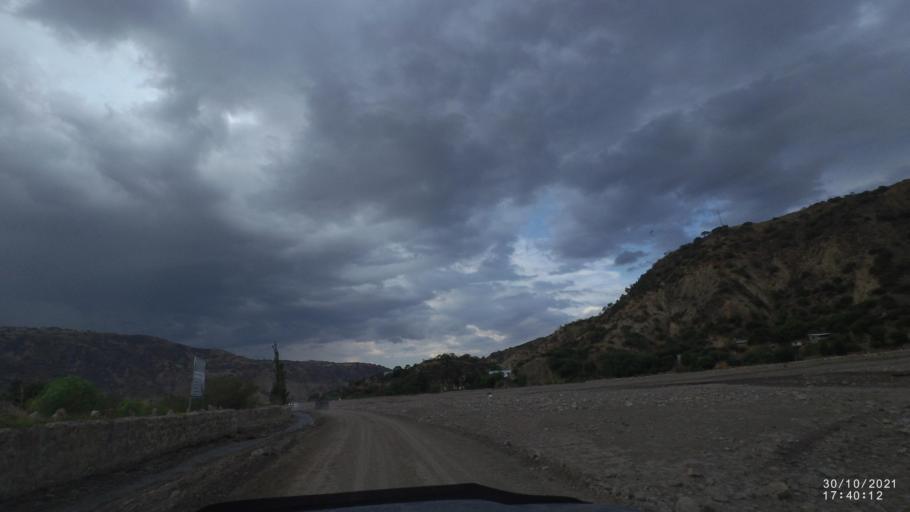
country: BO
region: Cochabamba
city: Sipe Sipe
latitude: -17.5308
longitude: -66.5507
